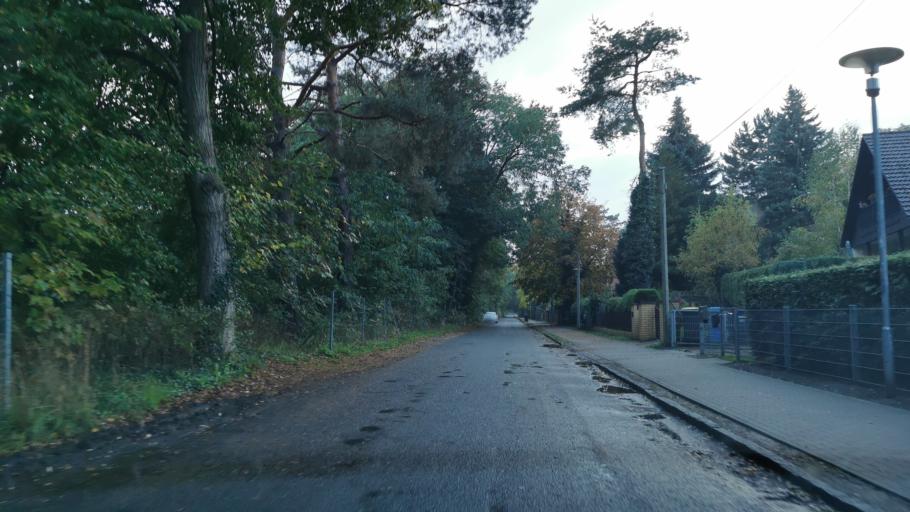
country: DE
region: Brandenburg
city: Michendorf
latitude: 52.3311
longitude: 13.0650
